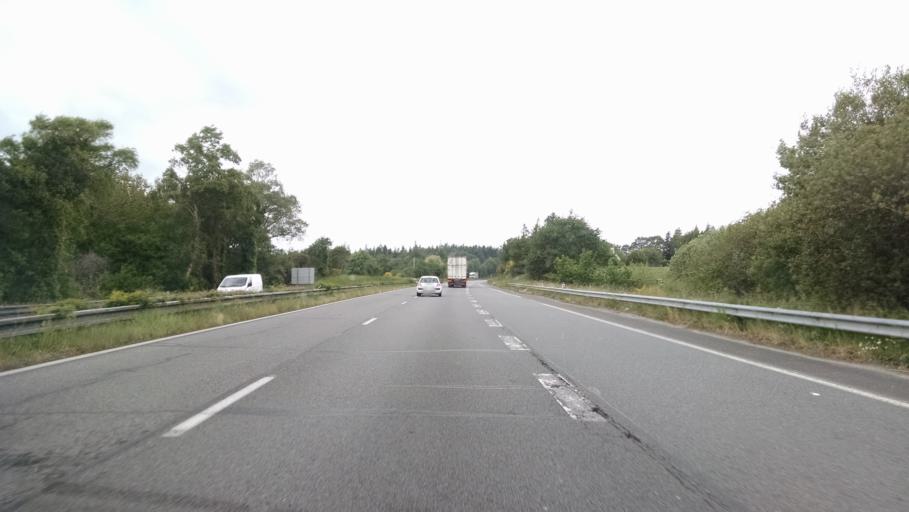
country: FR
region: Brittany
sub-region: Departement du Finistere
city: Quimperle
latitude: 47.8496
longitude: -3.5129
